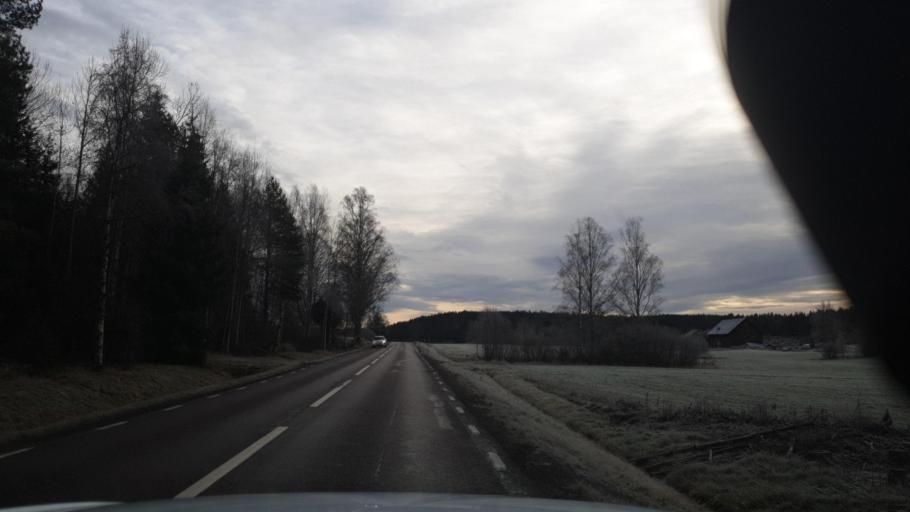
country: SE
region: Vaermland
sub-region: Sunne Kommun
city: Sunne
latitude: 59.6664
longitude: 12.9990
